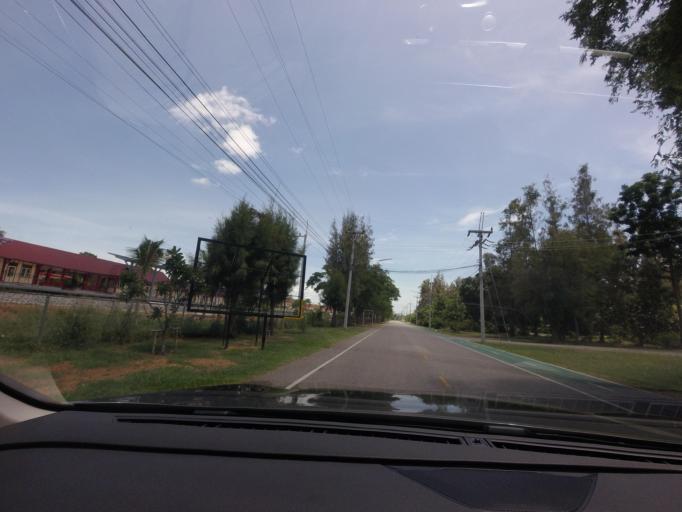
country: TH
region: Prachuap Khiri Khan
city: Hua Hin
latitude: 12.4995
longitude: 99.9728
